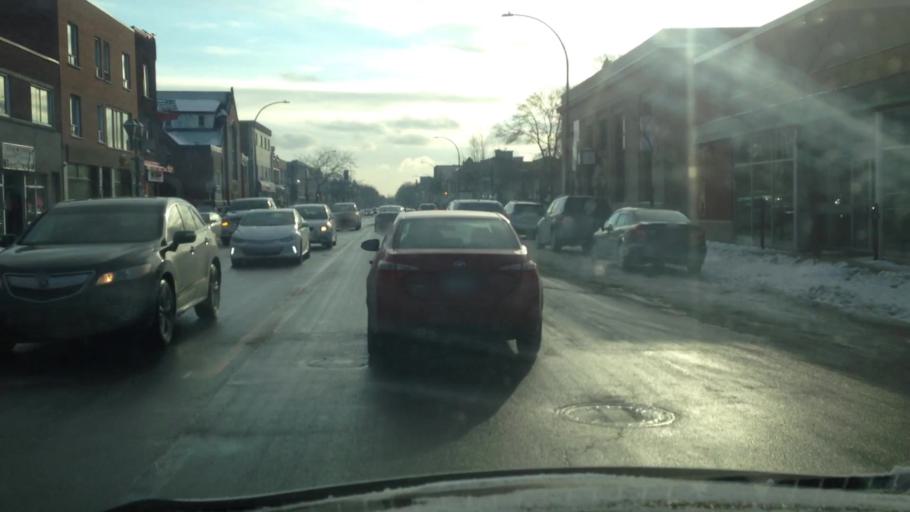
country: CA
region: Quebec
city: Mont-Royal
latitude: 45.5285
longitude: -73.6233
